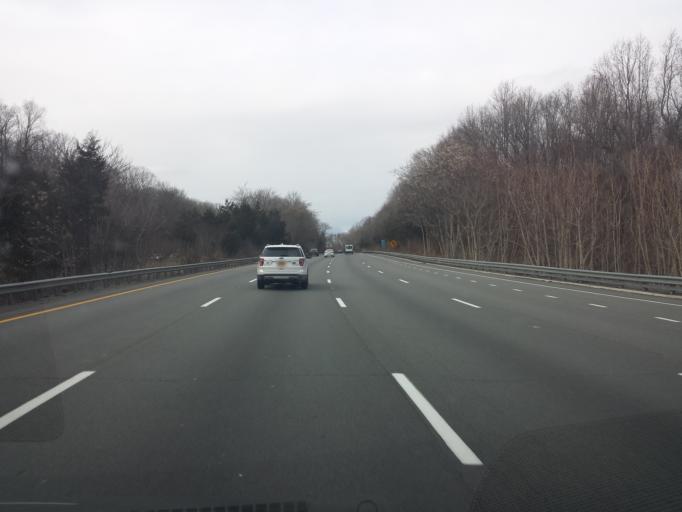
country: US
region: New Jersey
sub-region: Warren County
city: Oxford
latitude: 40.9255
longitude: -74.9619
